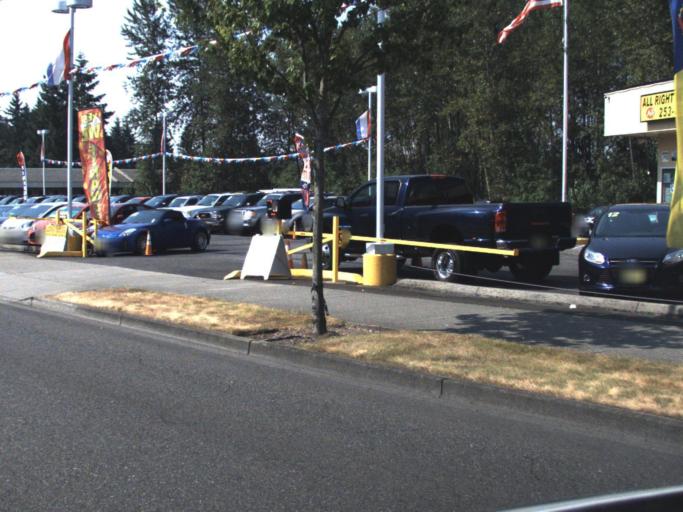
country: US
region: Washington
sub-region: King County
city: Federal Way
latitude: 47.3028
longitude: -122.3135
